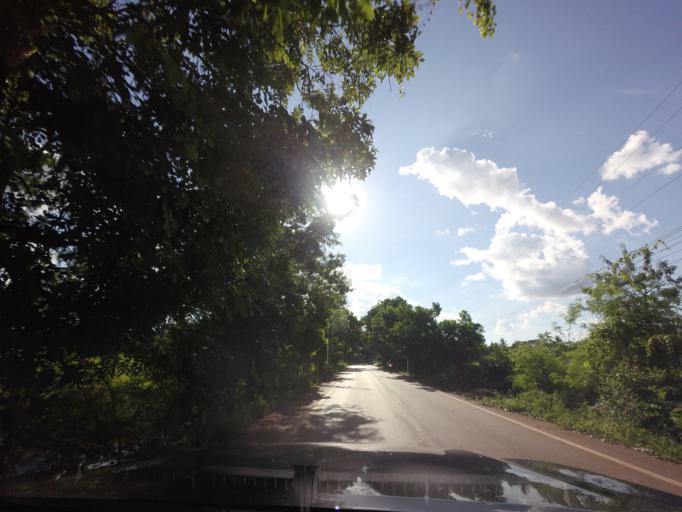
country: TH
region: Changwat Udon Thani
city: Ban Dung
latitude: 17.7462
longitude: 103.3324
